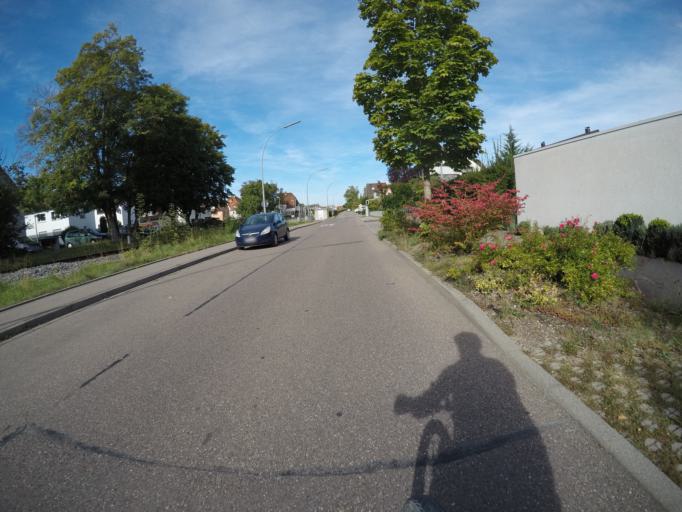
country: DE
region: Baden-Wuerttemberg
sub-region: Regierungsbezirk Stuttgart
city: Schwieberdingen
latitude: 48.8549
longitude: 9.0977
